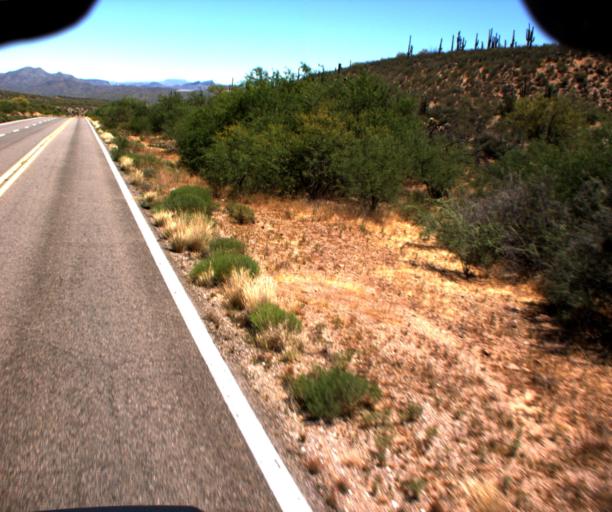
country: US
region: Arizona
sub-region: Pinal County
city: Kearny
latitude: 33.1323
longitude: -110.7825
